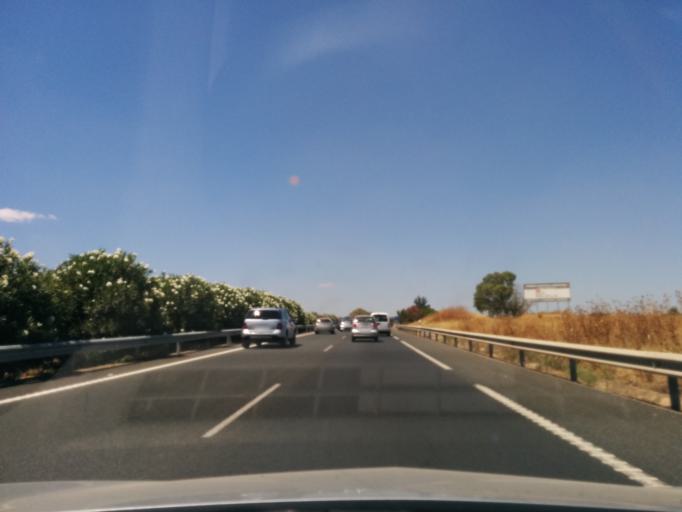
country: ES
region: Andalusia
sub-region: Provincia de Sevilla
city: Carrion de los Cespedes
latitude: 37.3611
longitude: -6.2778
